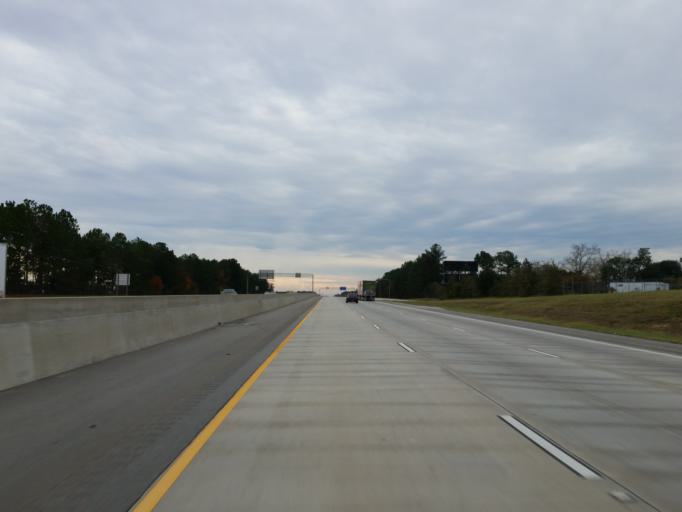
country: US
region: Georgia
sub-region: Cook County
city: Sparks
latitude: 31.2678
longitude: -83.4720
